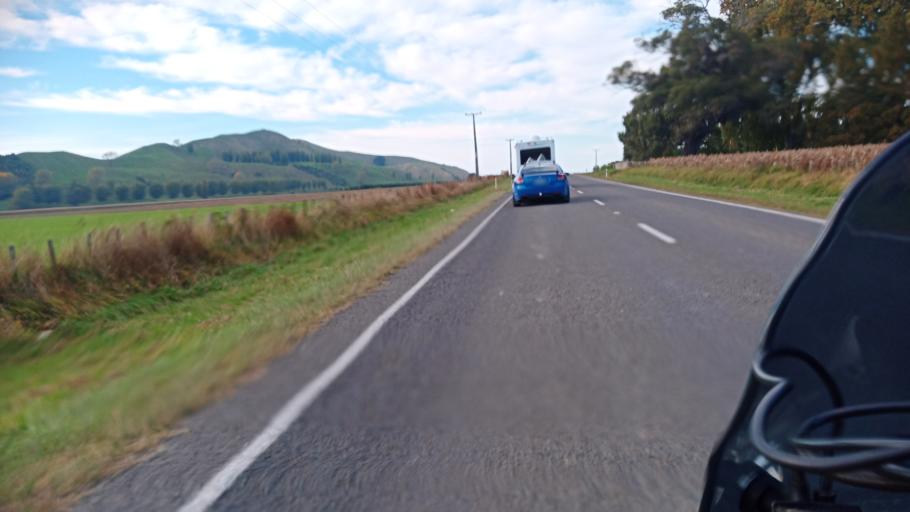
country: NZ
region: Gisborne
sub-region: Gisborne District
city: Gisborne
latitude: -38.7713
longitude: 177.9148
